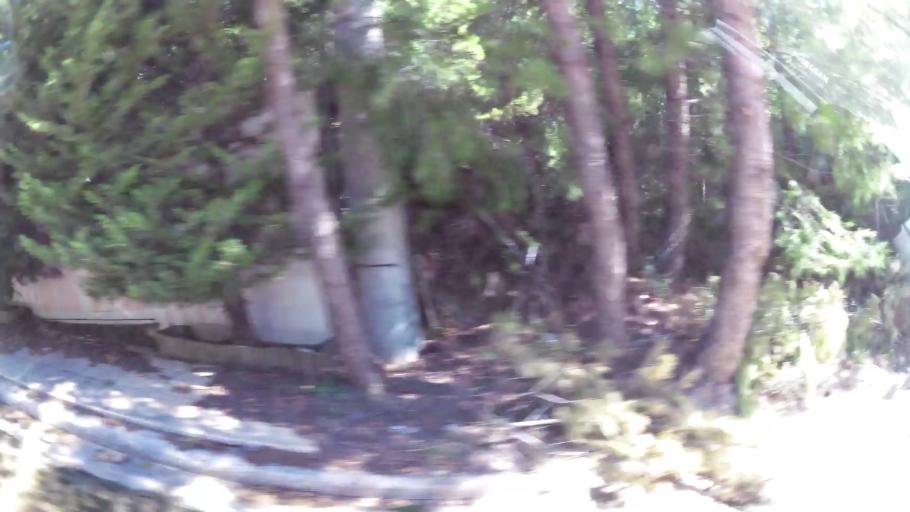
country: GR
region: Attica
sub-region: Nomarchia Anatolikis Attikis
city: Dioni
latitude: 38.0232
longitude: 23.9289
